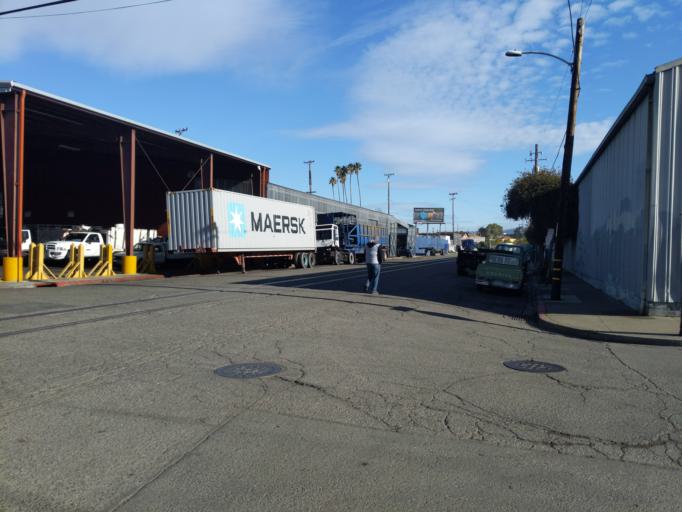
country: US
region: California
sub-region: Alameda County
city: Emeryville
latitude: 37.8209
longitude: -122.2854
